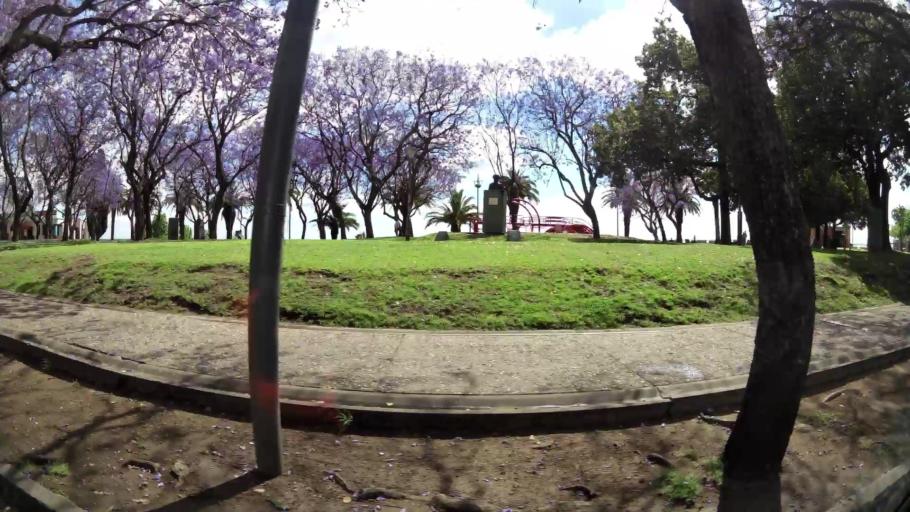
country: AR
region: Santa Fe
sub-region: Departamento de Rosario
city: Rosario
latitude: -32.9378
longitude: -60.6385
